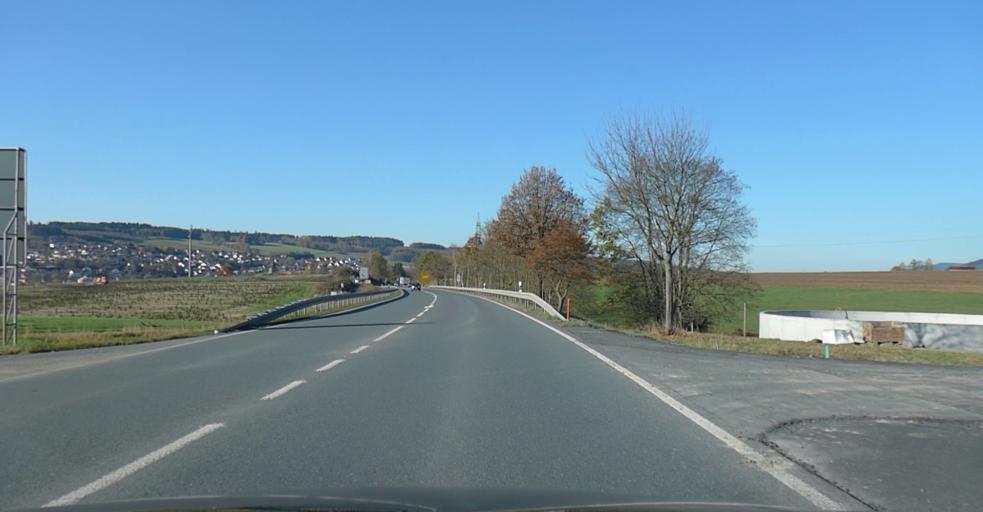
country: DE
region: Bavaria
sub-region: Upper Franconia
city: Untersteinach
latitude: 50.1304
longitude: 11.5454
